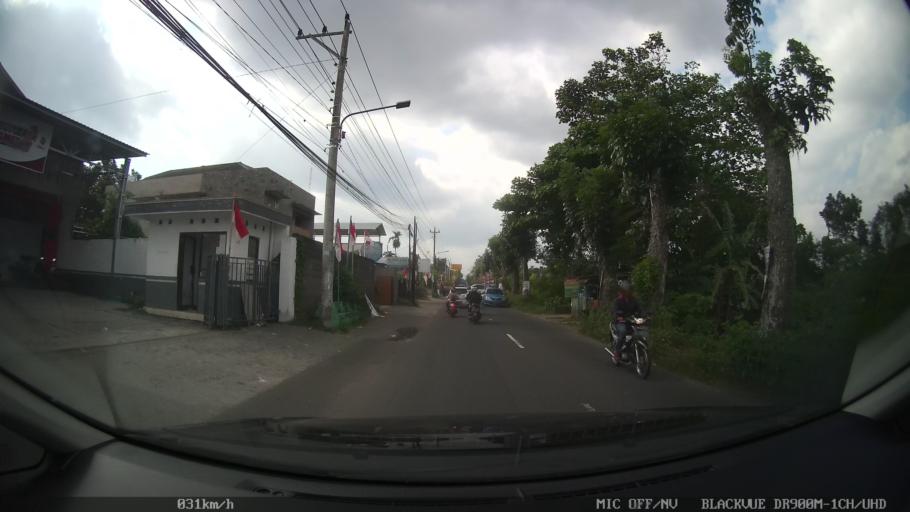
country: ID
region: Daerah Istimewa Yogyakarta
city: Melati
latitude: -7.7472
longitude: 110.3485
